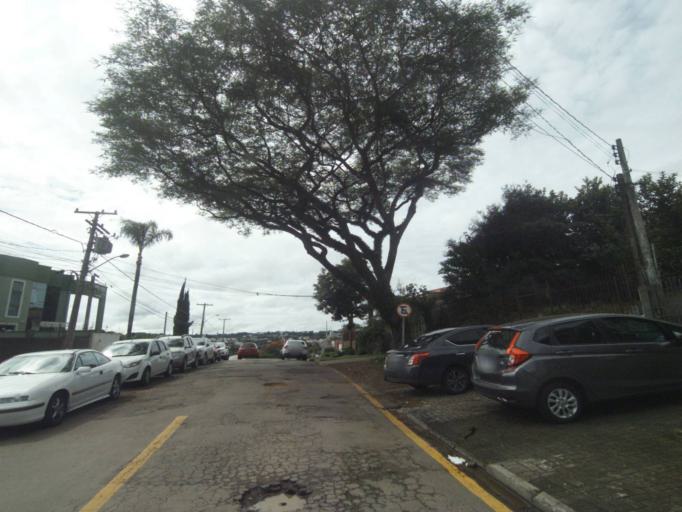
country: BR
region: Parana
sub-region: Curitiba
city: Curitiba
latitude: -25.4364
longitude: -49.3111
